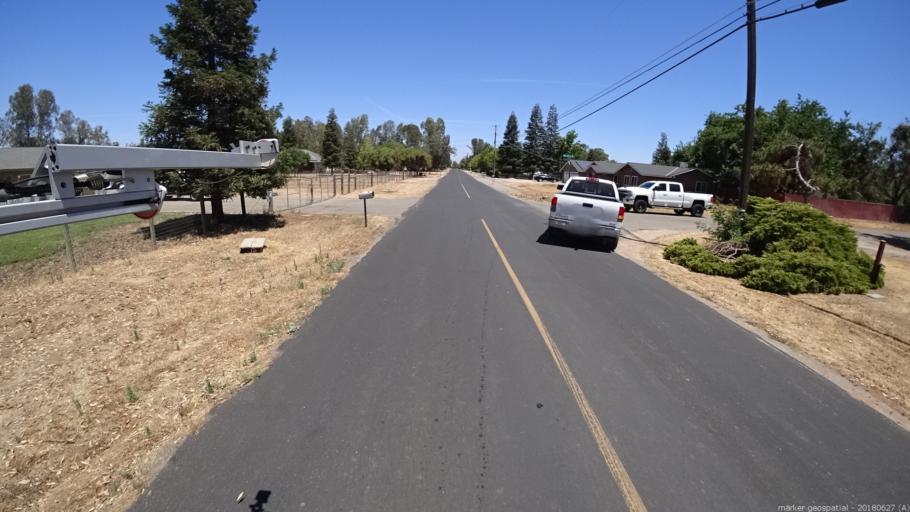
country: US
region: California
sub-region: Madera County
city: Bonadelle Ranchos-Madera Ranchos
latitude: 36.9285
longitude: -119.8736
